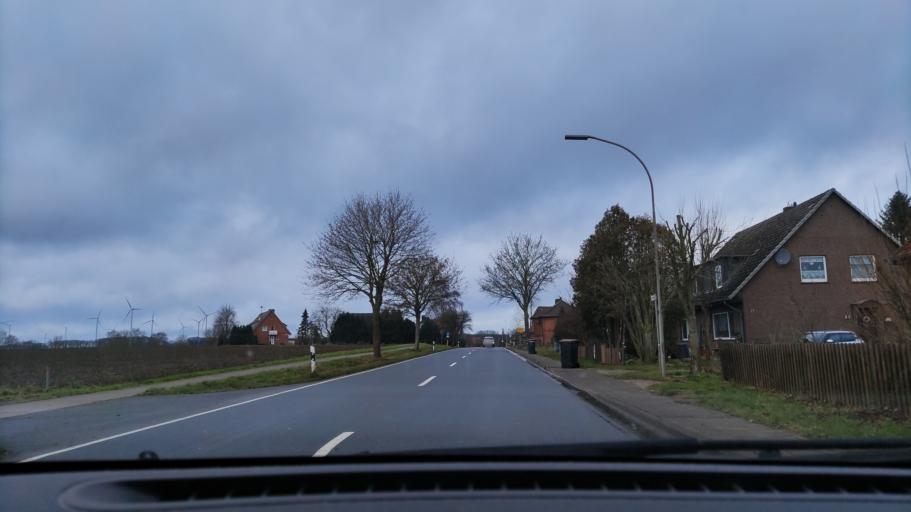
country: DE
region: Lower Saxony
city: Hanstedt Eins
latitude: 53.0408
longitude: 10.3812
